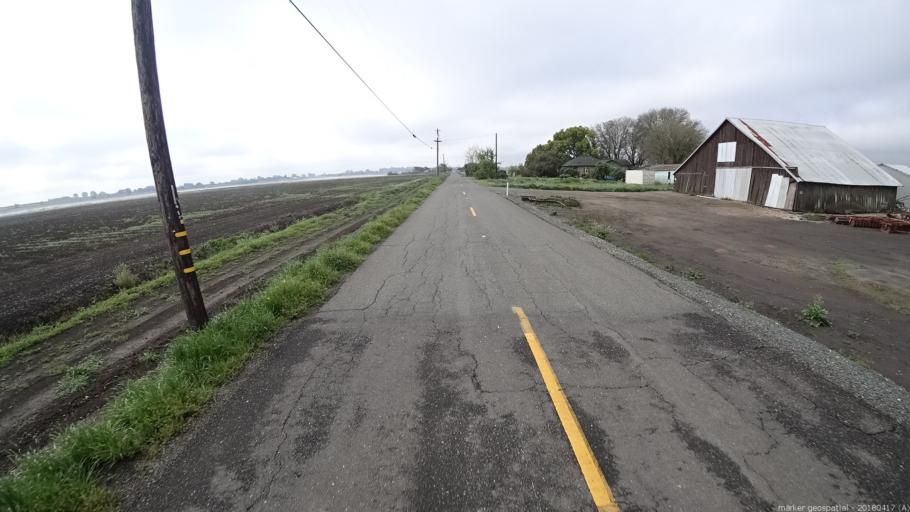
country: US
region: California
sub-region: Sacramento County
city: Walnut Grove
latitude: 38.2007
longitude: -121.5952
